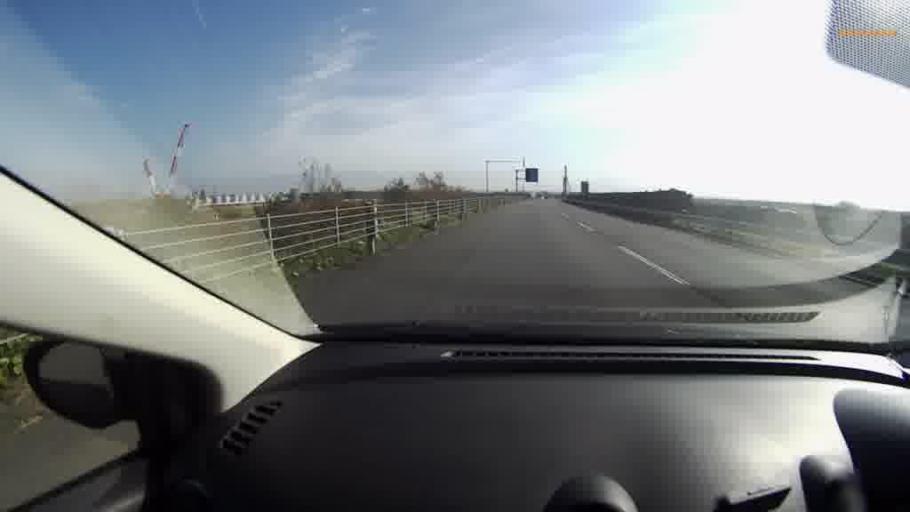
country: JP
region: Hokkaido
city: Kushiro
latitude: 43.0362
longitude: 144.3199
